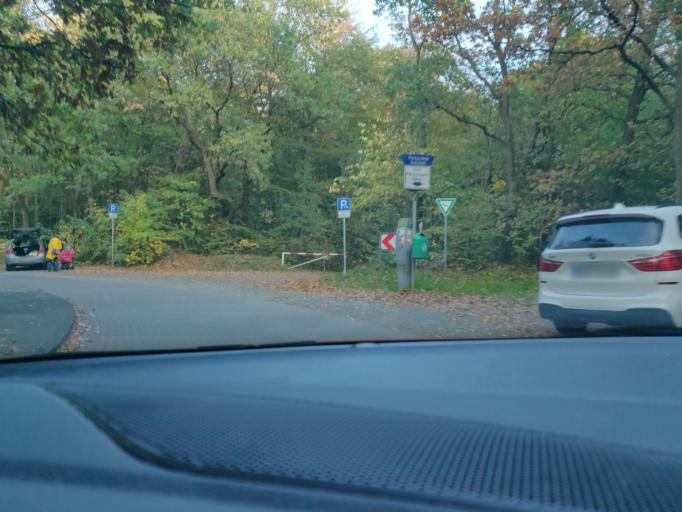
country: DE
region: Lower Saxony
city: Nordholz
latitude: 53.8585
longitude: 8.6013
